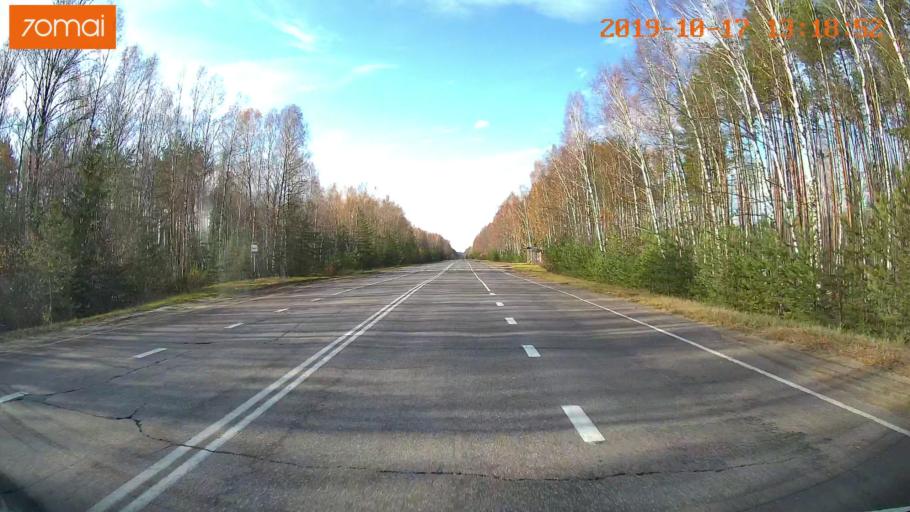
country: RU
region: Rjazan
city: Gus'-Zheleznyy
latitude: 55.0658
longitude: 41.0875
